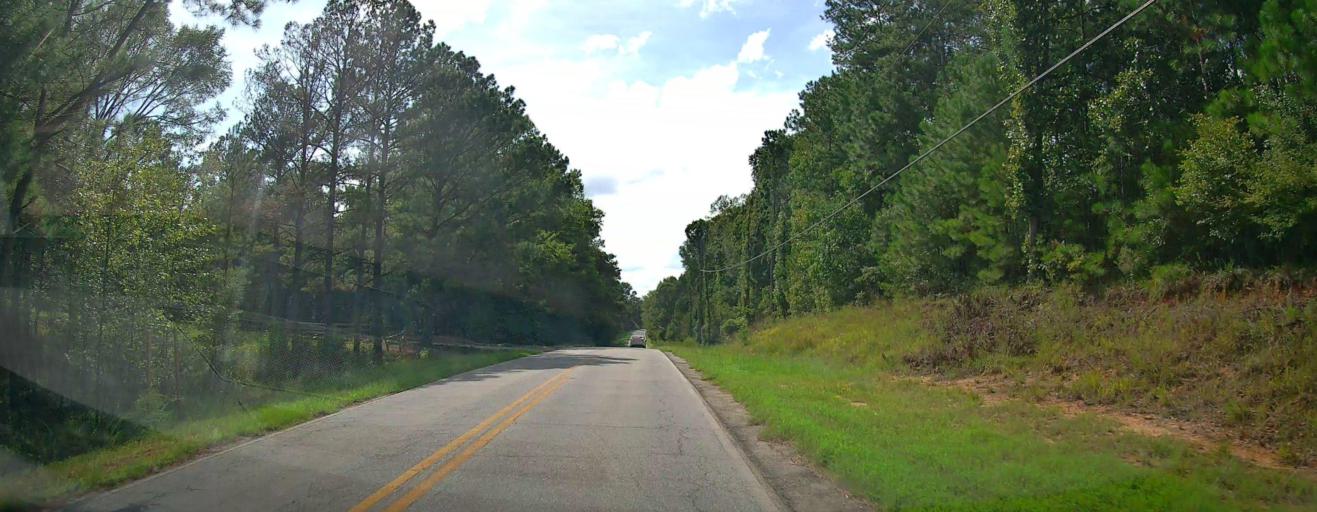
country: US
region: Alabama
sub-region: Russell County
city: Phenix City
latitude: 32.5905
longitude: -84.9303
